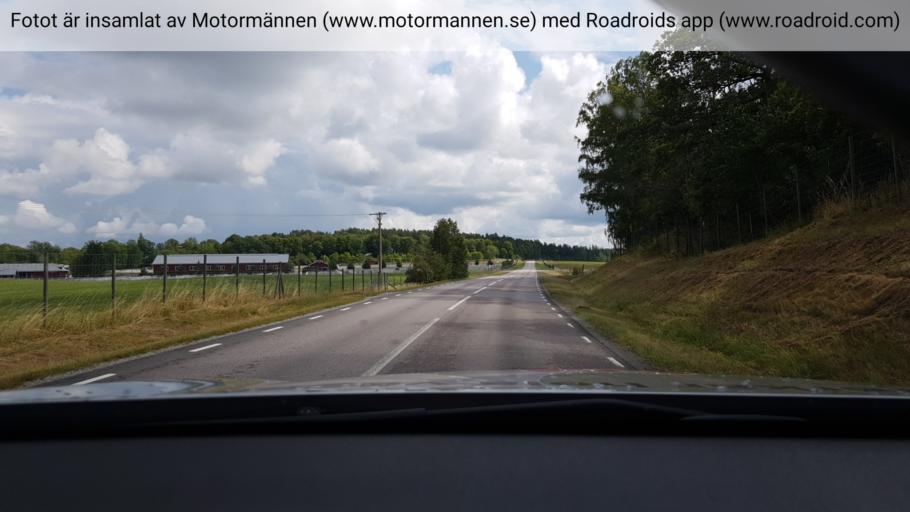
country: SE
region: Stockholm
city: Stenhamra
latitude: 59.3473
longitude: 17.6294
